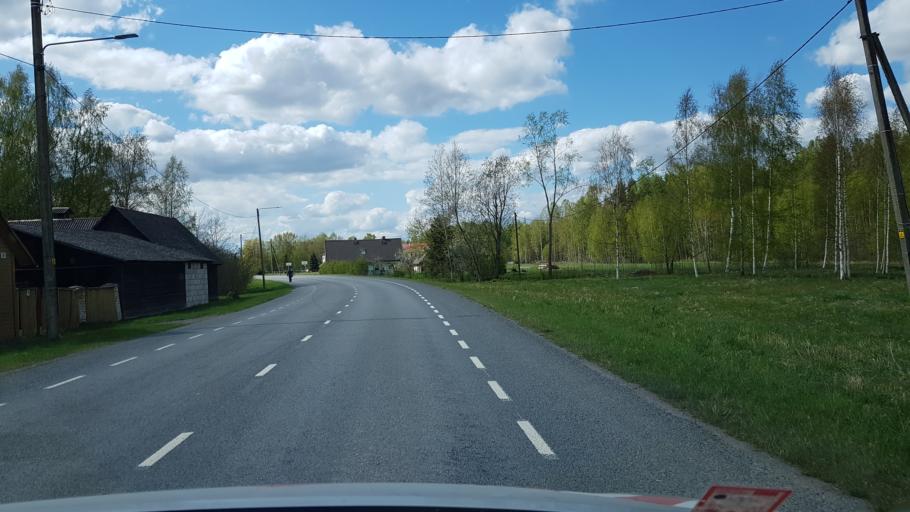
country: EE
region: Polvamaa
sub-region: Polva linn
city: Polva
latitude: 58.2813
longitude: 27.0565
